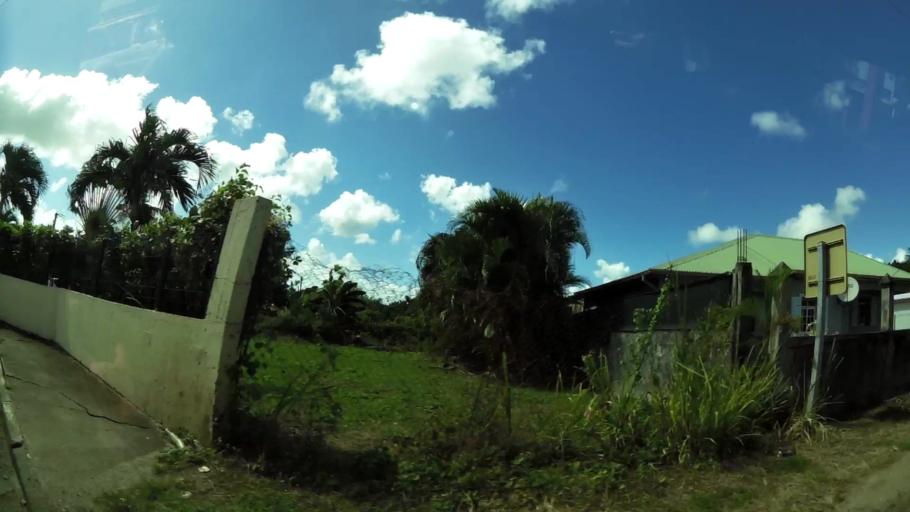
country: GP
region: Guadeloupe
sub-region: Guadeloupe
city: Petit-Canal
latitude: 16.3701
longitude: -61.4516
